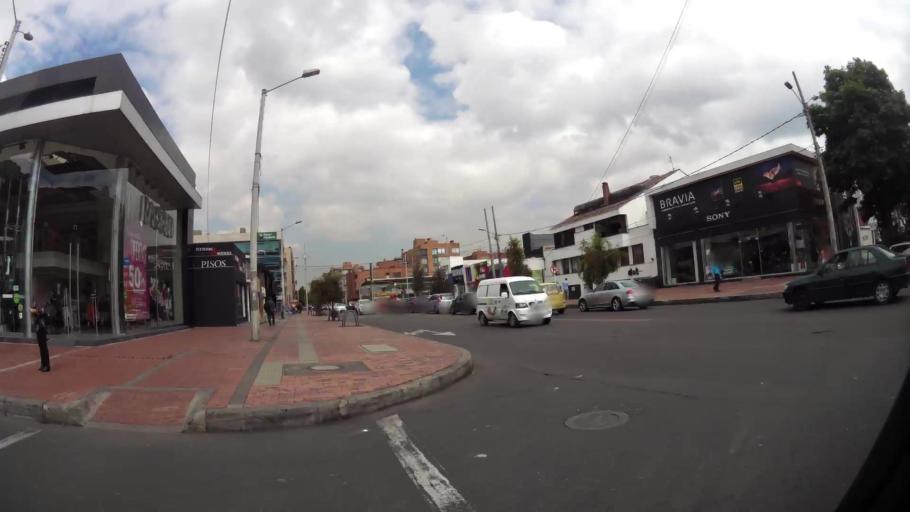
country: CO
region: Bogota D.C.
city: Barrio San Luis
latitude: 4.7016
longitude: -74.0486
